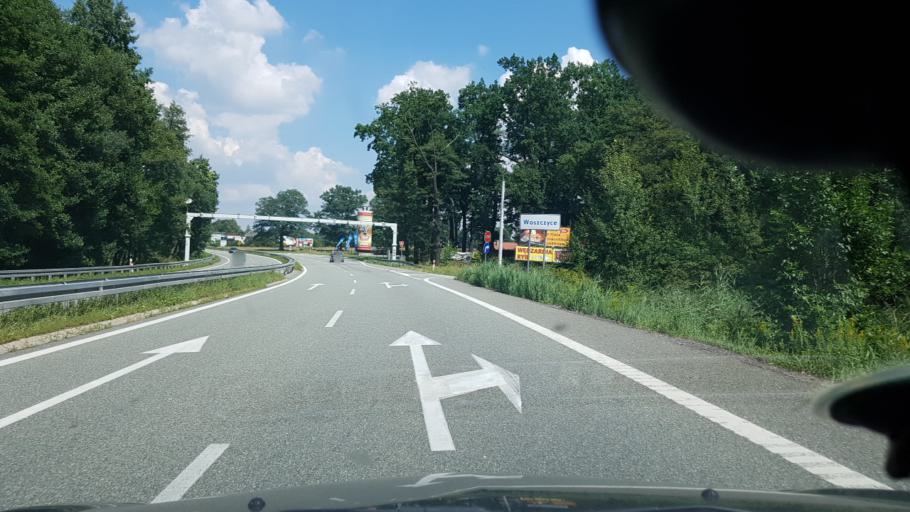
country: PL
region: Silesian Voivodeship
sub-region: Powiat pszczynski
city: Rudziczka
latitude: 50.0787
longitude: 18.7520
